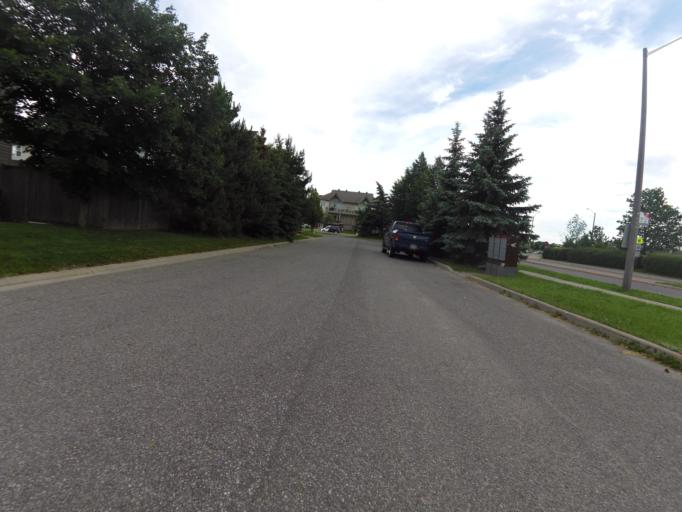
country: CA
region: Ontario
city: Ottawa
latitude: 45.2866
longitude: -75.7082
